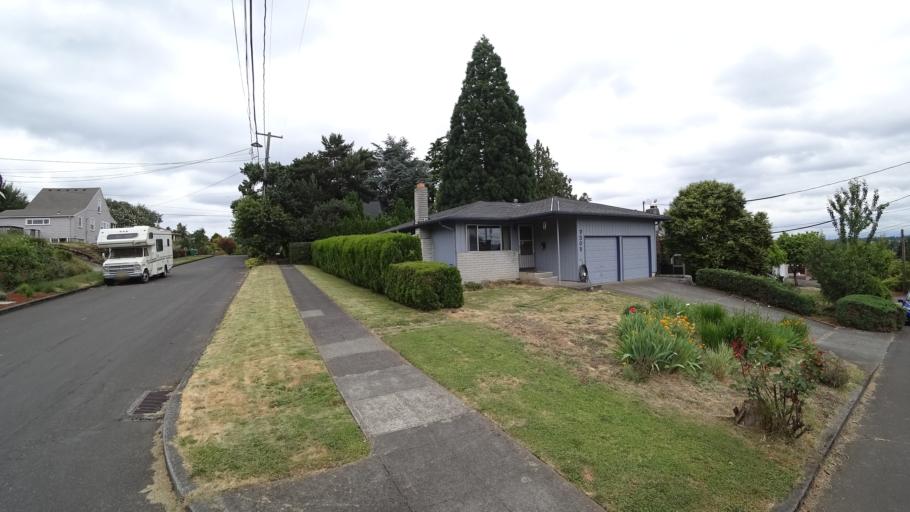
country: US
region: Oregon
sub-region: Multnomah County
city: Lents
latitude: 45.5123
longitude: -122.5876
